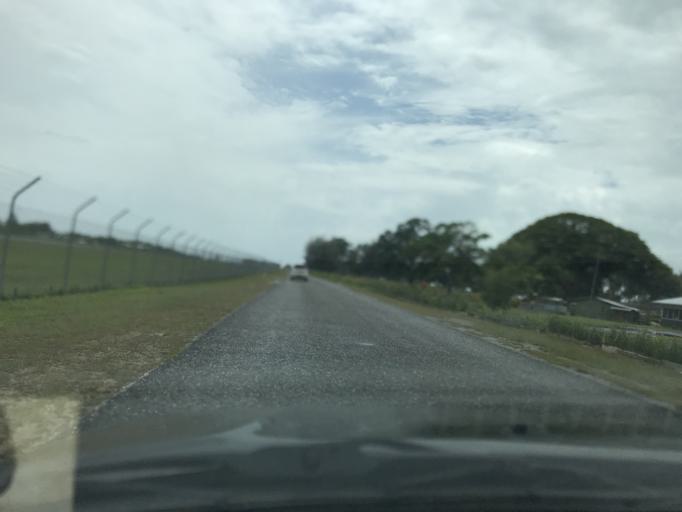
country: SB
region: Western Province
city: Gizo
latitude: -8.3276
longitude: 157.2546
